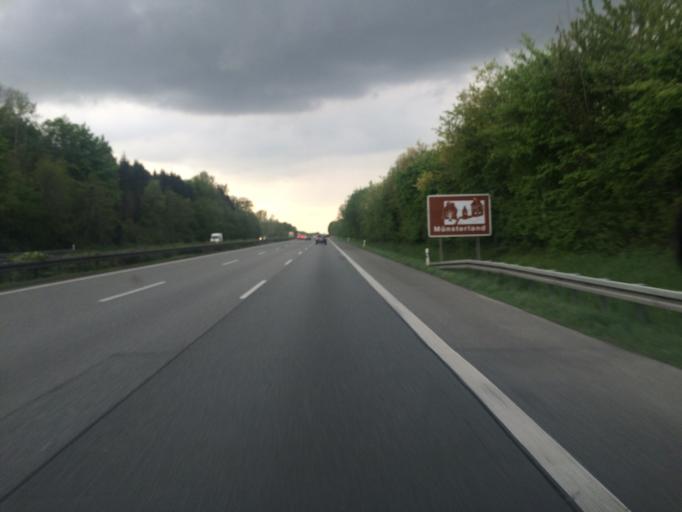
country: DE
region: North Rhine-Westphalia
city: Oelde
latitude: 51.8198
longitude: 8.1733
